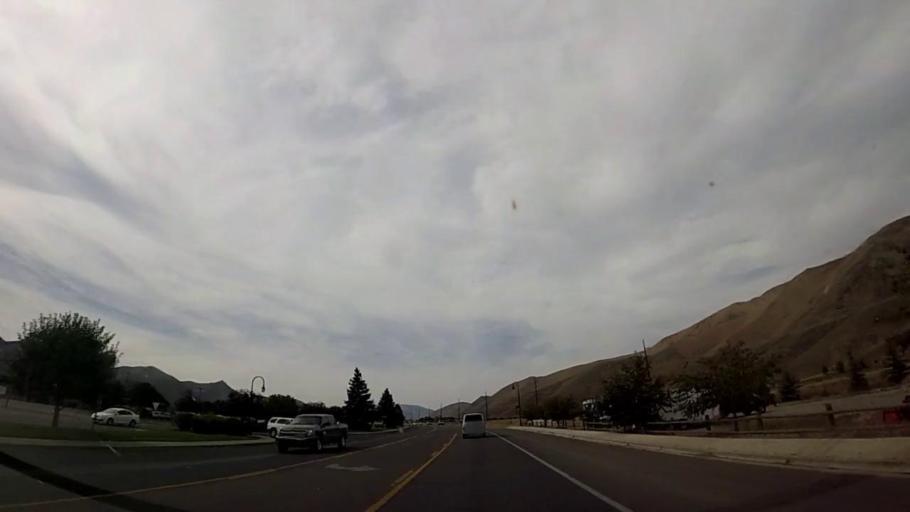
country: US
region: Idaho
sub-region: Blaine County
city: Bellevue
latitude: 43.4734
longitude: -114.2649
